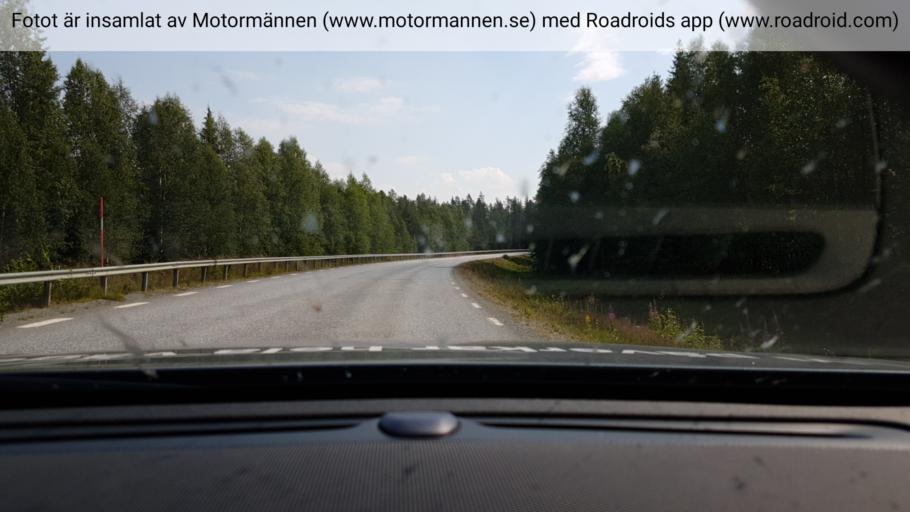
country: SE
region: Vaesterbotten
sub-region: Storumans Kommun
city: Fristad
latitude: 65.4194
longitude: 16.3043
